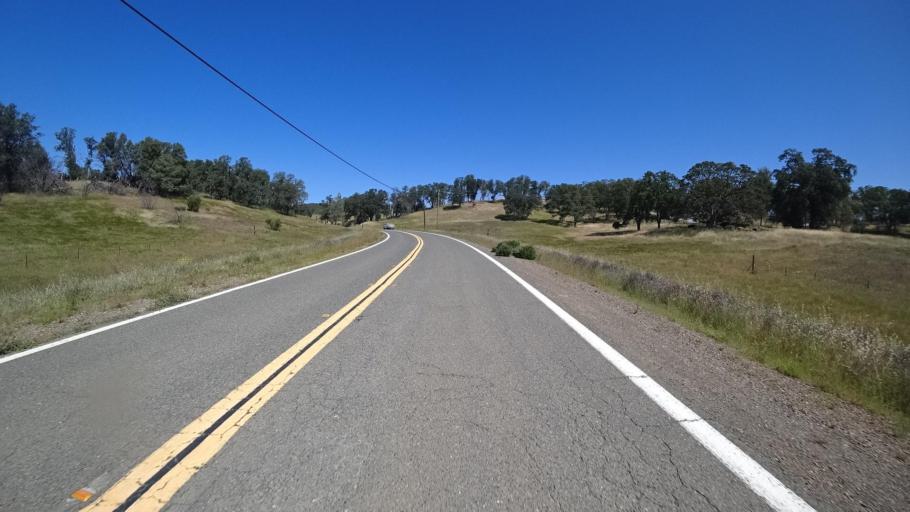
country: US
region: California
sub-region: Lake County
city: Hidden Valley Lake
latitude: 38.8740
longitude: -122.4216
